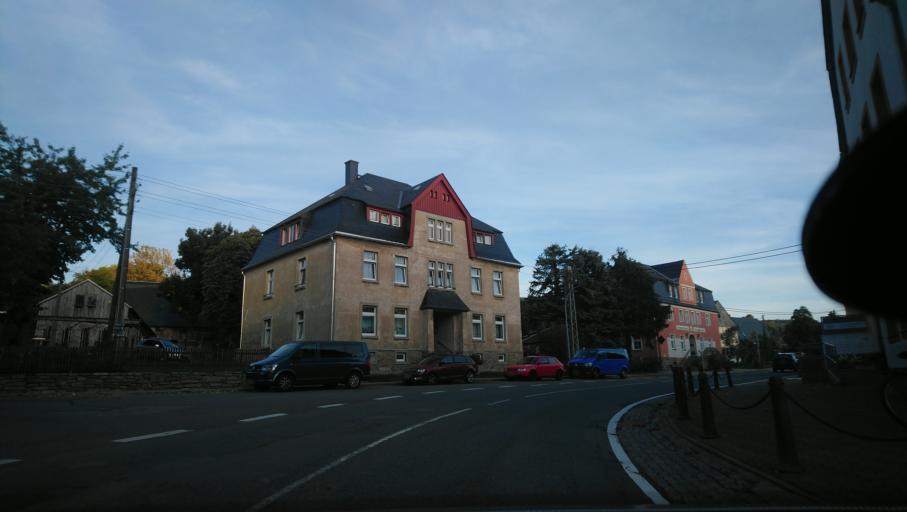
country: DE
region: Saxony
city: Konigswalde
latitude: 50.5464
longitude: 13.0488
